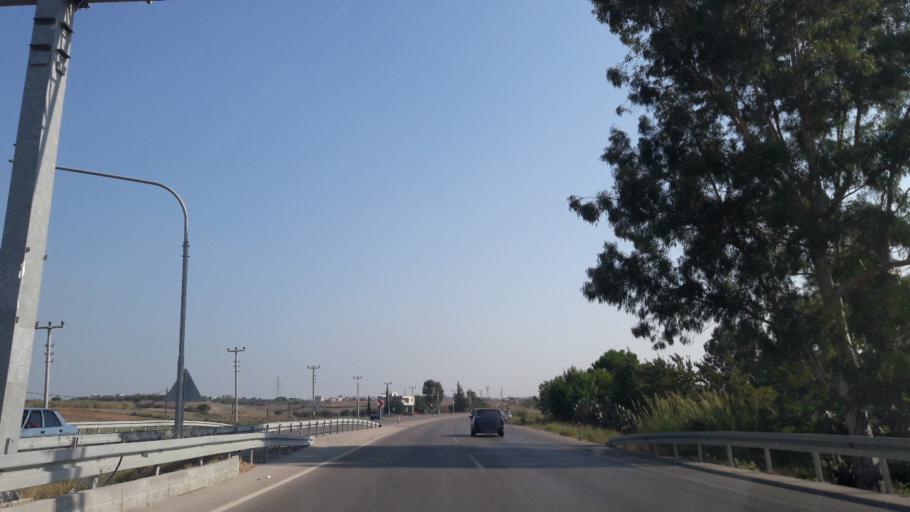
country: TR
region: Adana
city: Yuregir
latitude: 37.0634
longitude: 35.4461
